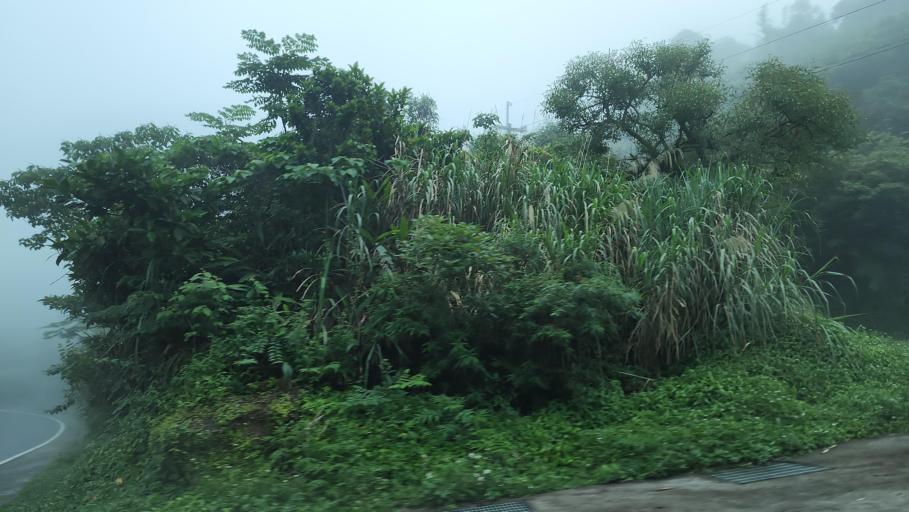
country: TW
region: Taipei
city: Taipei
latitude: 25.1396
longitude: 121.6028
